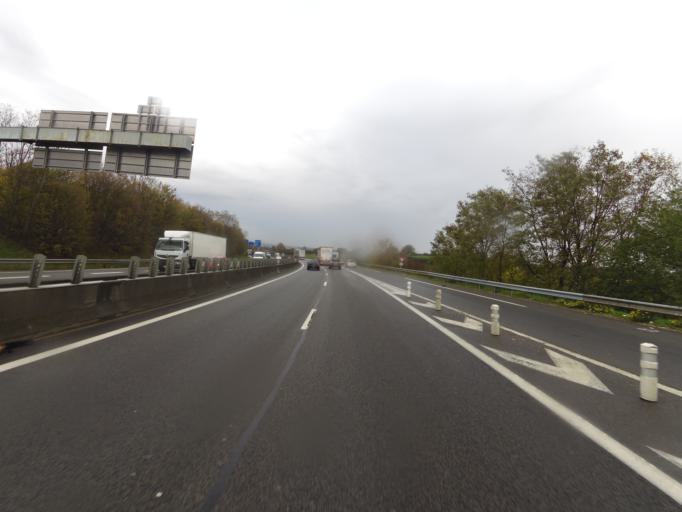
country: FR
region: Rhone-Alpes
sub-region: Departement du Rhone
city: Saint-Priest
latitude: 45.6930
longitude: 4.9689
